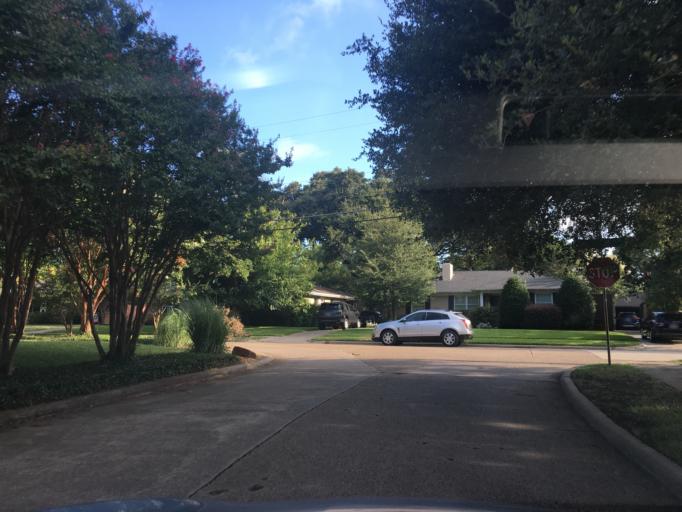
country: US
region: Texas
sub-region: Dallas County
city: Highland Park
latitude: 32.8488
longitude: -96.7517
